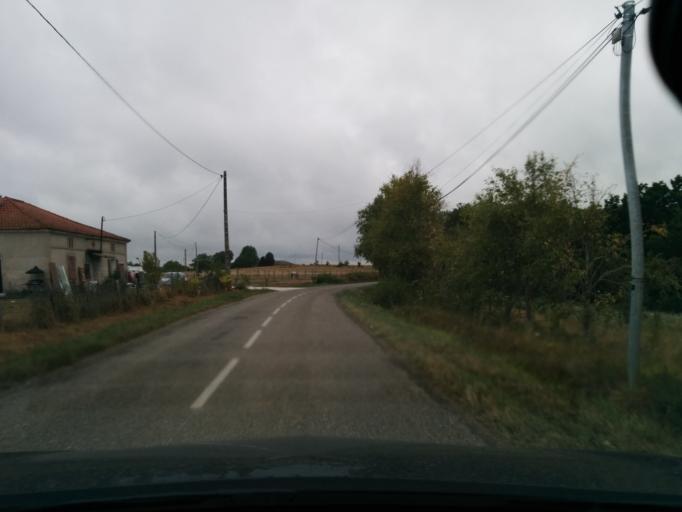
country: FR
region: Midi-Pyrenees
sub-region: Departement du Tarn-et-Garonne
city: Moissac
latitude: 44.1554
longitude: 1.0636
